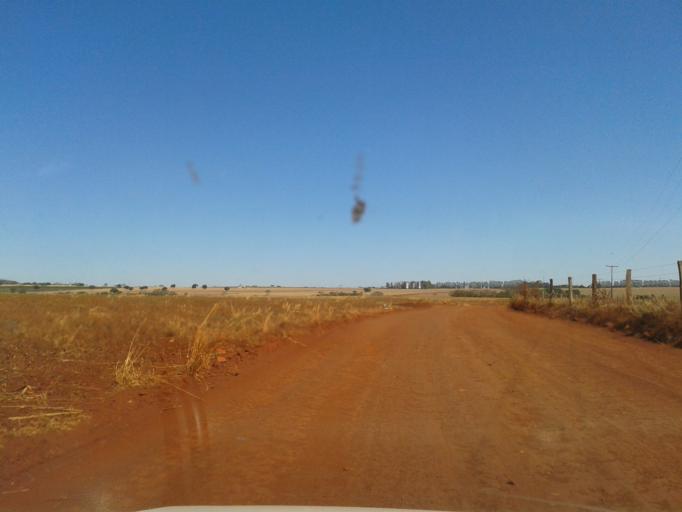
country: BR
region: Minas Gerais
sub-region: Centralina
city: Centralina
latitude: -18.5916
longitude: -49.1701
